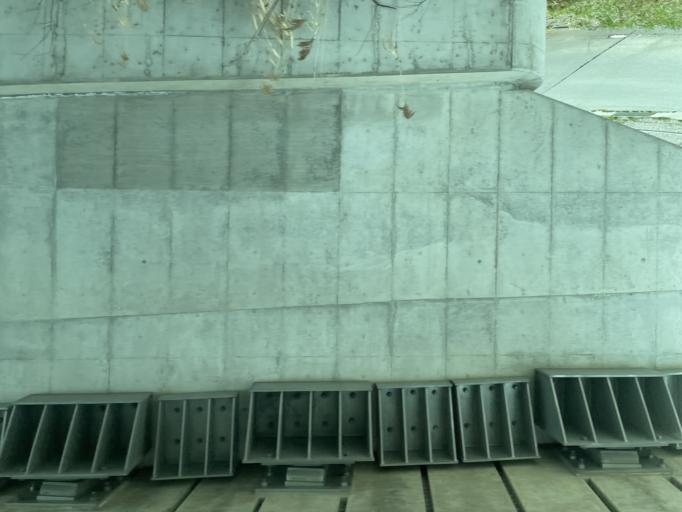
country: JP
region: Aomori
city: Goshogawara
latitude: 40.7637
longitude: 140.4352
